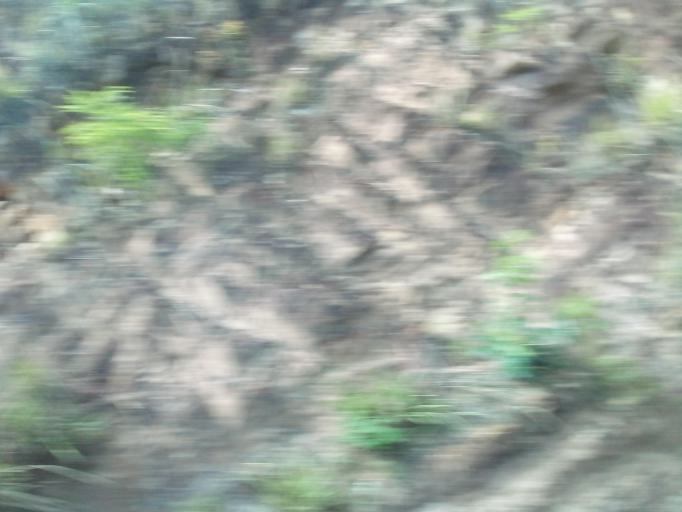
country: BR
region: Minas Gerais
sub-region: Caete
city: Caete
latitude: -19.8909
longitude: -43.7468
